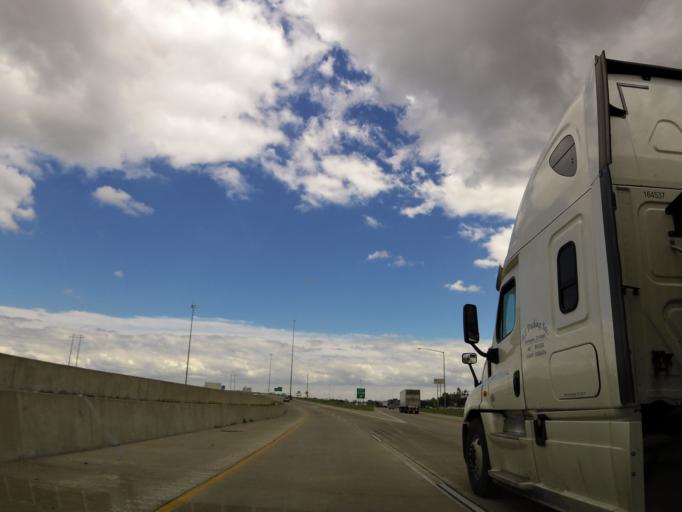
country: US
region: Arkansas
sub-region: Crittenden County
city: West Memphis
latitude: 35.1558
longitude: -90.1517
